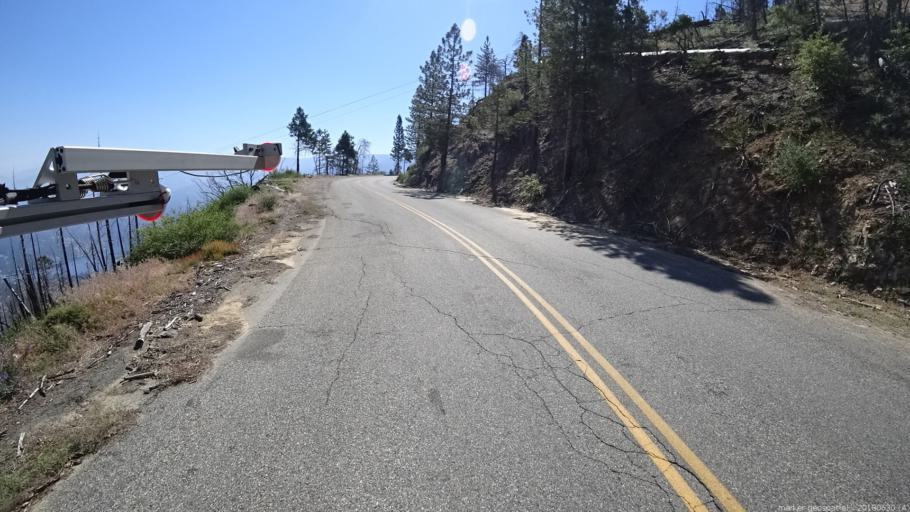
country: US
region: California
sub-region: Fresno County
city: Auberry
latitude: 37.3125
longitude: -119.3500
